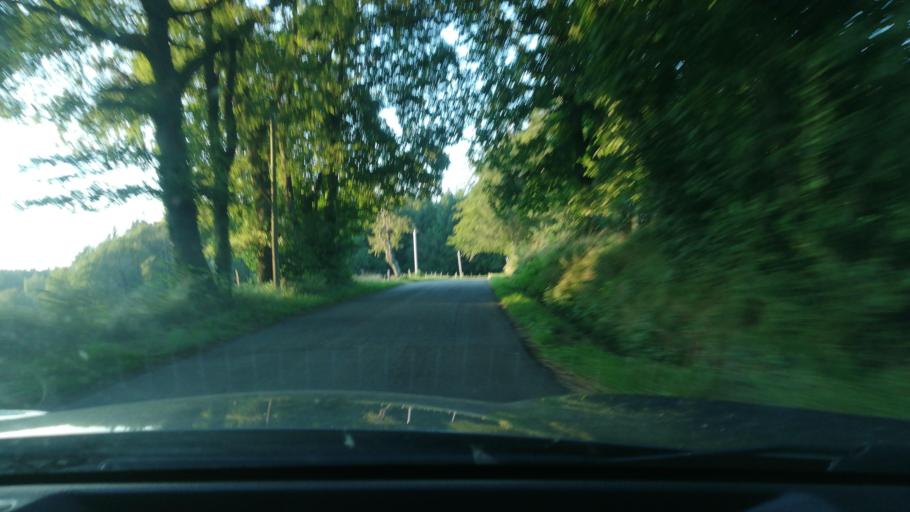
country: FR
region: Midi-Pyrenees
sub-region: Departement du Lot
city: Saint-Cere
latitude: 44.8850
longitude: 2.0279
